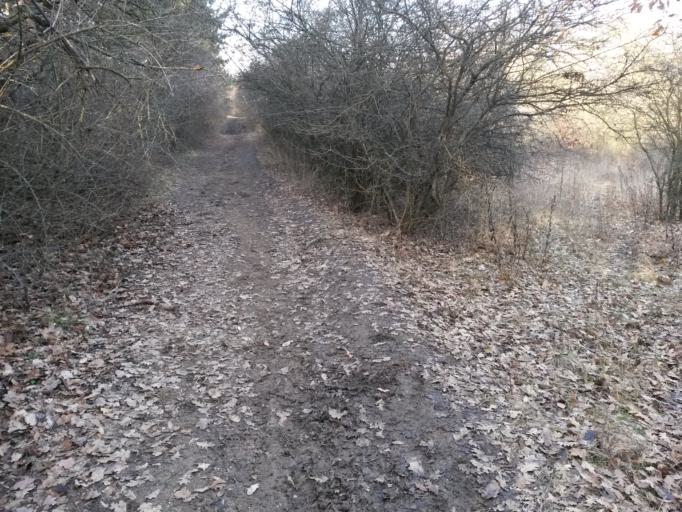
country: HU
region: Pest
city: Zsambek
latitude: 47.5744
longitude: 18.7172
